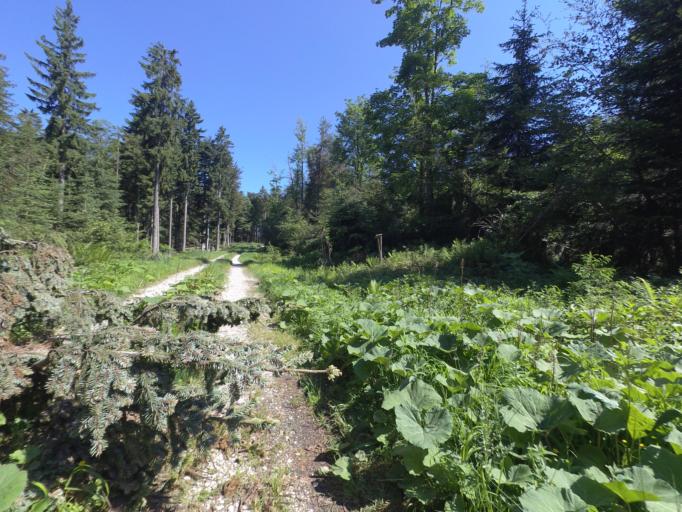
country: AT
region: Salzburg
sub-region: Politischer Bezirk Salzburg-Umgebung
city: Elsbethen
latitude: 47.7494
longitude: 13.1224
